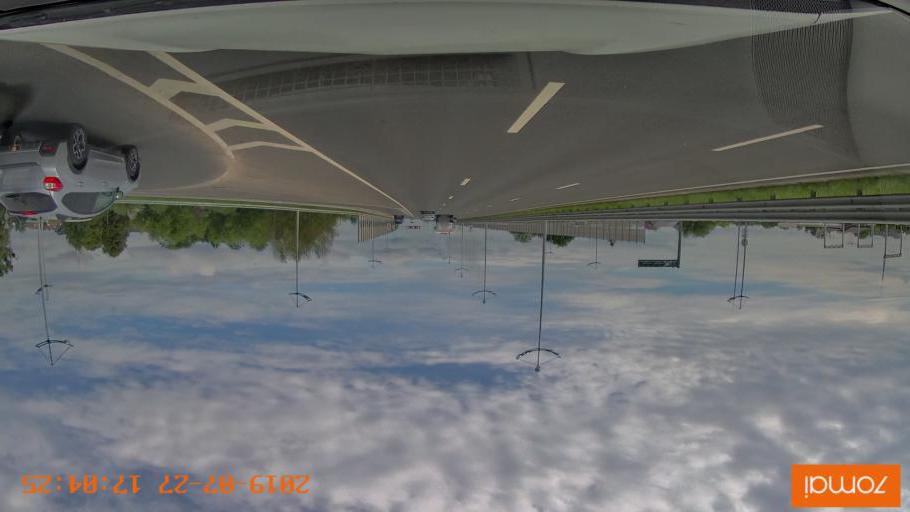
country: RU
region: Kaliningrad
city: Bol'shoe Isakovo
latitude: 54.7138
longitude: 20.5968
